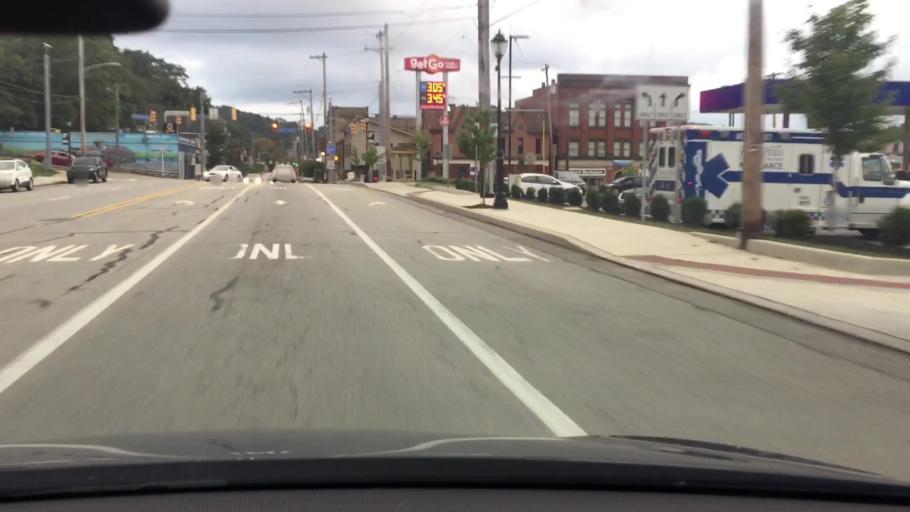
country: US
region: Pennsylvania
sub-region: Allegheny County
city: Verona
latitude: 40.5086
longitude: -79.8428
